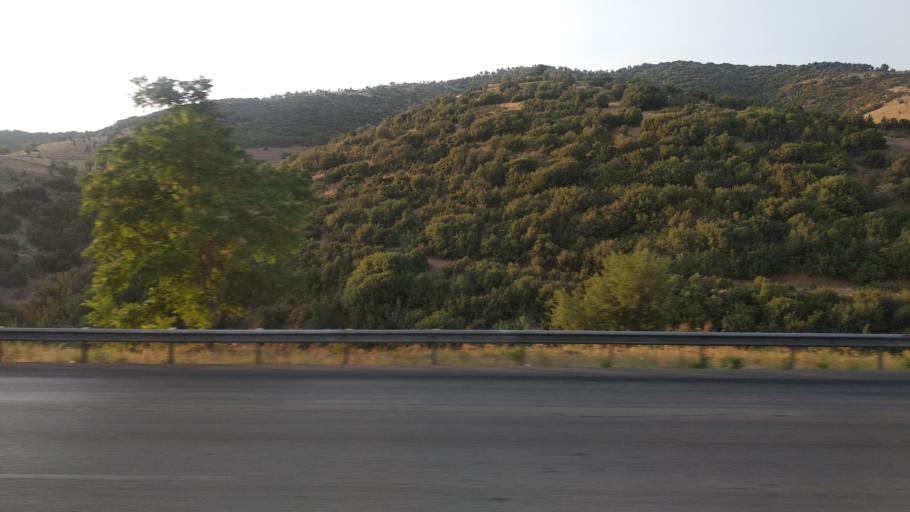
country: TR
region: Manisa
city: Menye
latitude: 38.5510
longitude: 28.4607
